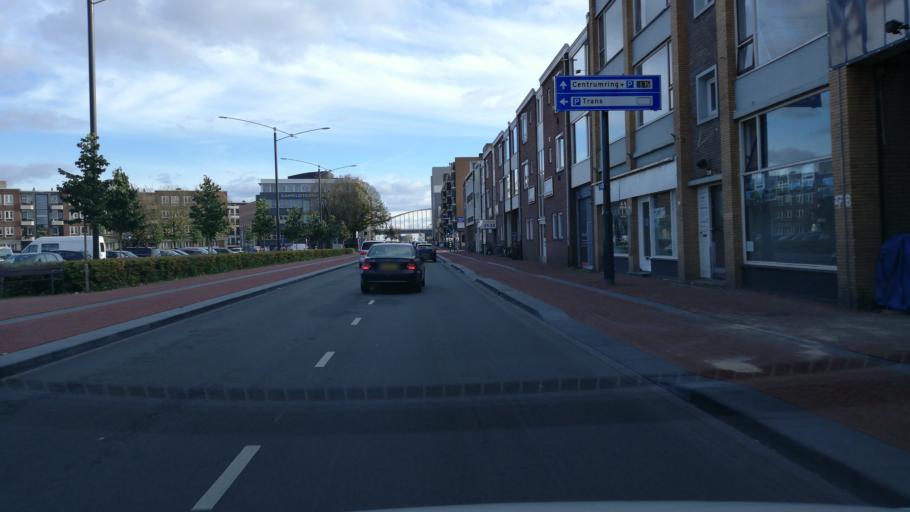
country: NL
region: Gelderland
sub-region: Gemeente Arnhem
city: Arnhem
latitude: 51.9786
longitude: 5.9061
